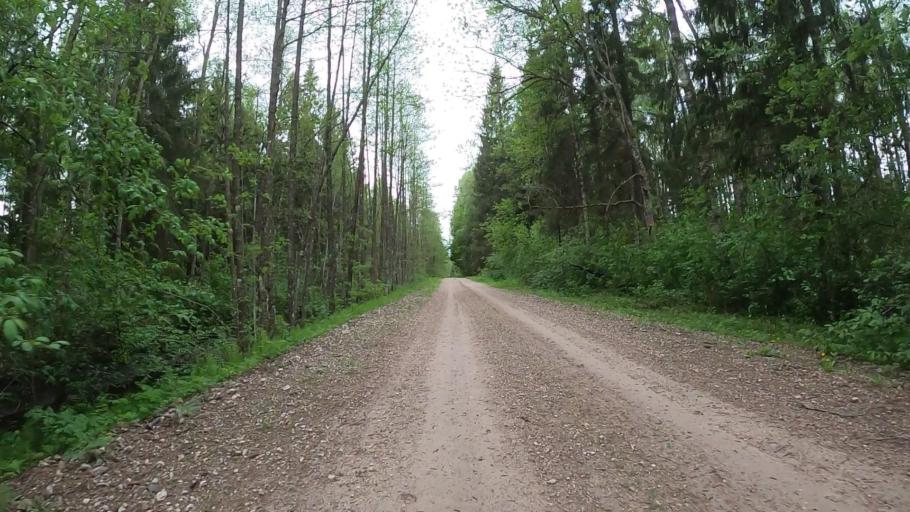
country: LV
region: Ozolnieku
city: Ozolnieki
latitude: 56.7982
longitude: 23.7816
